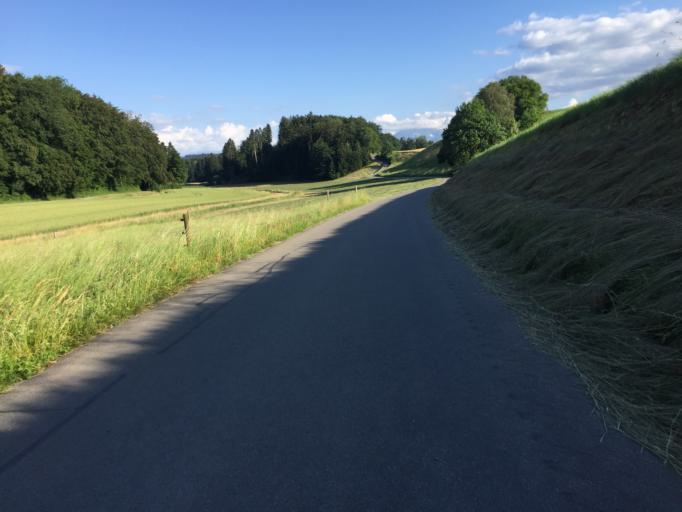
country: CH
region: Bern
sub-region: Bern-Mittelland District
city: Niederwichtrach
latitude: 46.8405
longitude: 7.5819
